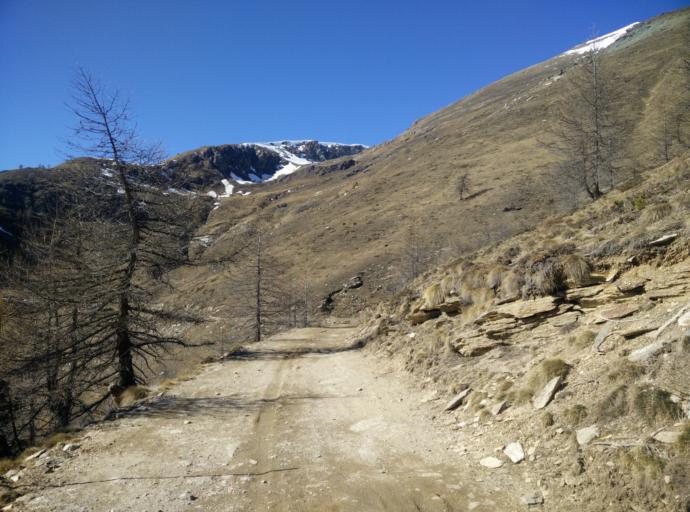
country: IT
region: Piedmont
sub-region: Provincia di Torino
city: Roure
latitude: 45.0450
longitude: 7.1119
